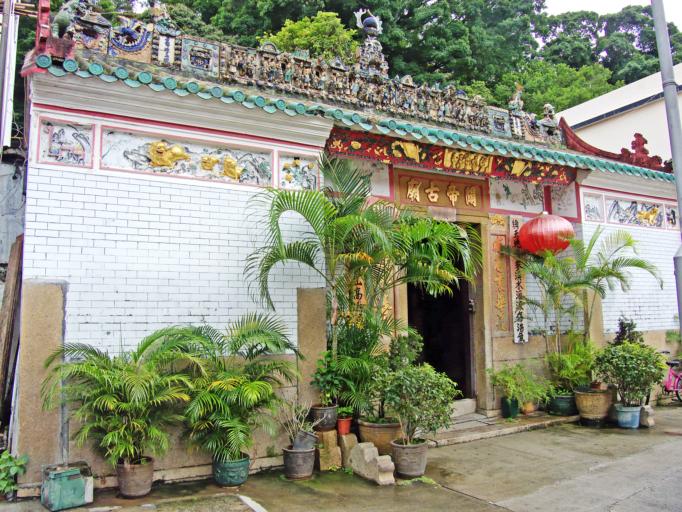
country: HK
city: Tai O
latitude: 22.2546
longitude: 113.8621
